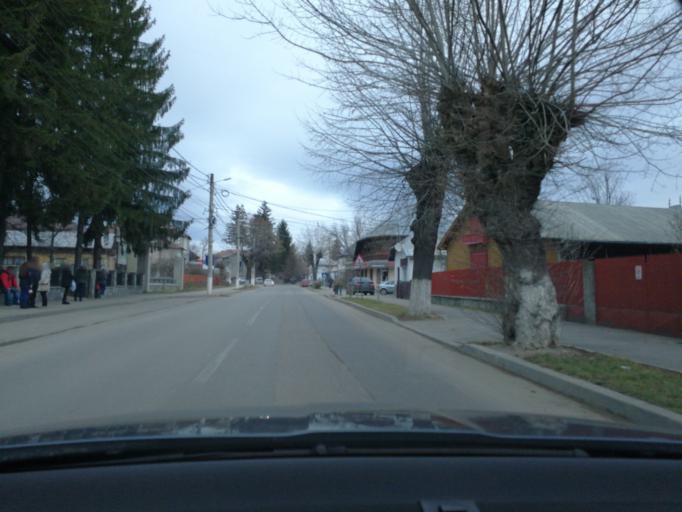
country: RO
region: Prahova
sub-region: Oras Breaza
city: Breaza de Jos
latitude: 45.1740
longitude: 25.6722
